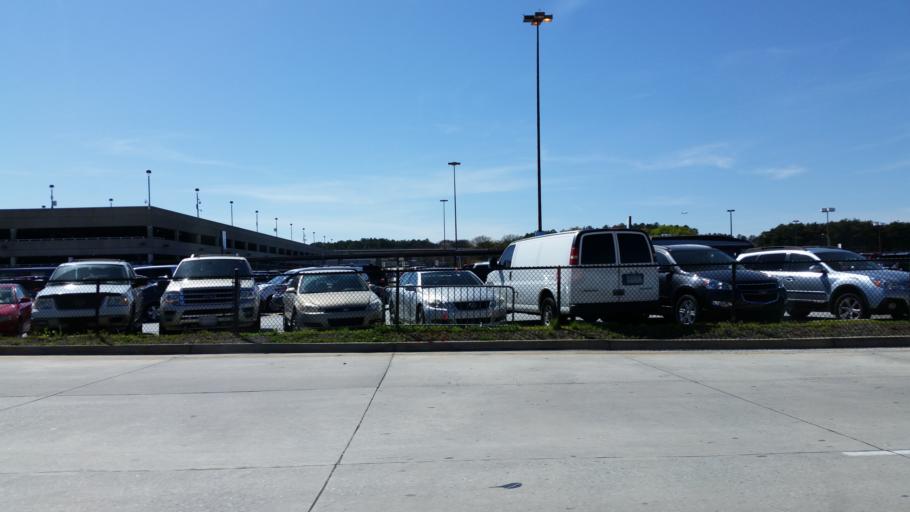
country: US
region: Georgia
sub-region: Fulton County
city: College Park
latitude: 33.6441
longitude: -84.4426
